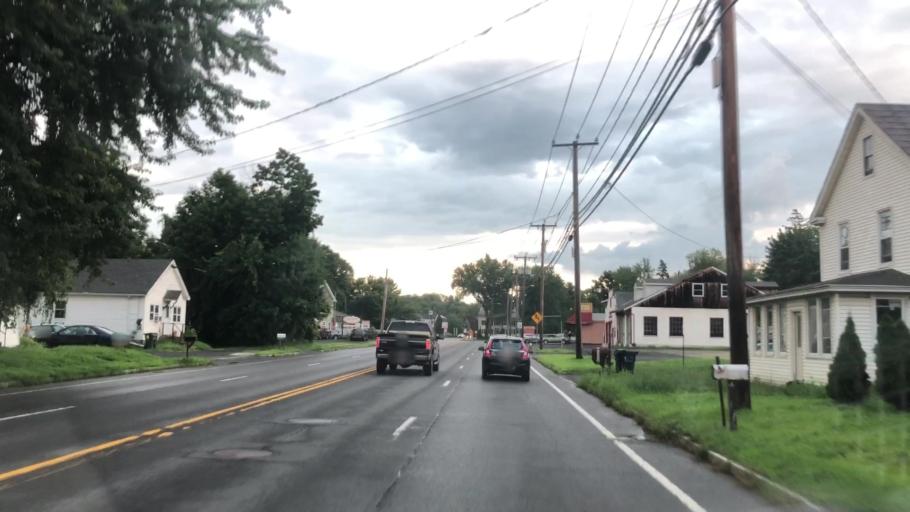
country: US
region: Massachusetts
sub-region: Hampshire County
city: Hadley
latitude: 42.3412
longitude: -72.5992
